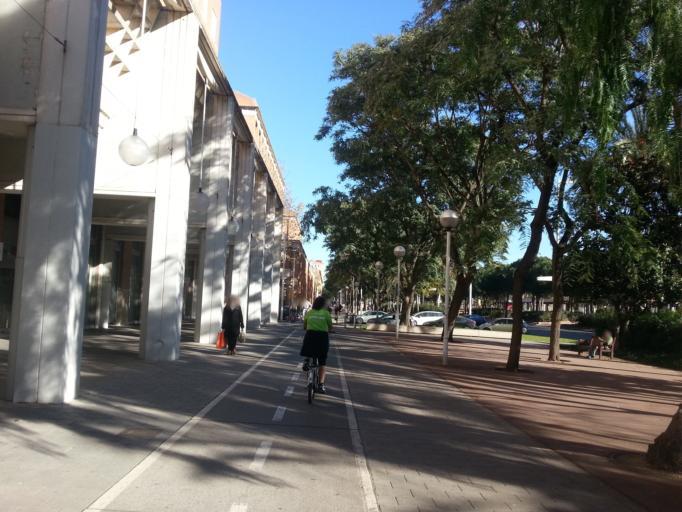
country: ES
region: Catalonia
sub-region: Provincia de Barcelona
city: Ciutat Vella
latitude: 41.3895
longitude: 2.1975
